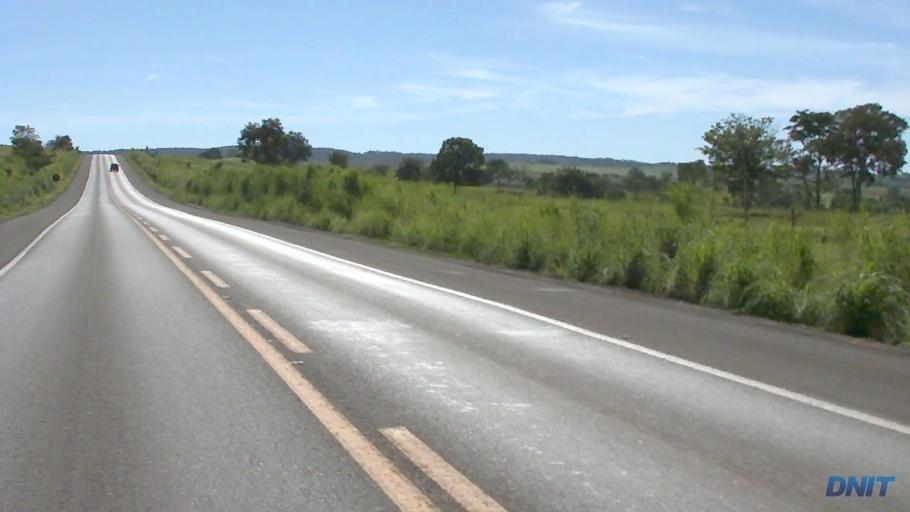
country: BR
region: Goias
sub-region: Padre Bernardo
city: Padre Bernardo
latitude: -15.2199
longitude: -48.5190
